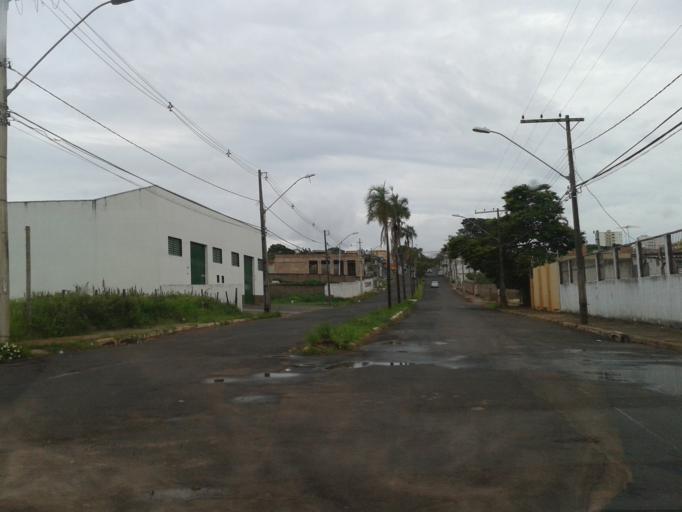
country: BR
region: Minas Gerais
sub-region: Uberlandia
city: Uberlandia
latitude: -18.9339
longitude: -48.2456
